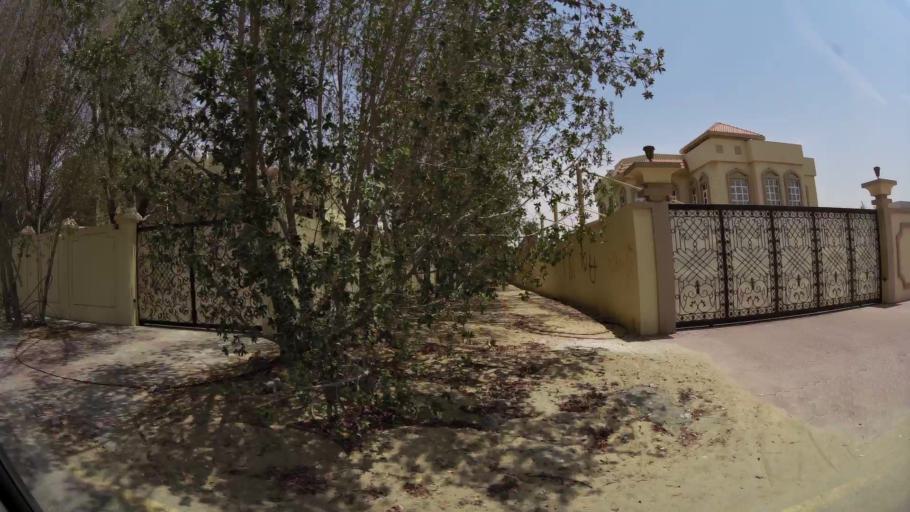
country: AE
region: Ash Shariqah
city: Sharjah
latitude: 25.2474
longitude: 55.4625
